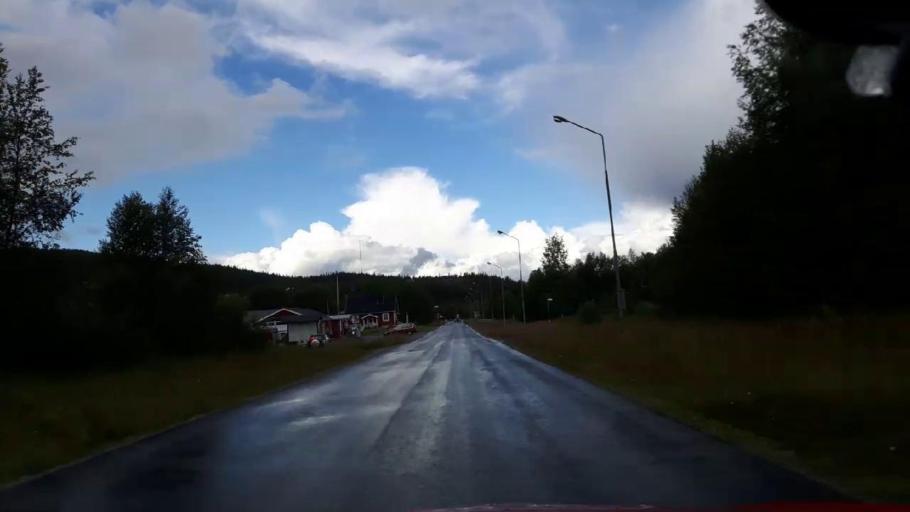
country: SE
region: Vaesterbotten
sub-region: Vilhelmina Kommun
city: Sjoberg
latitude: 64.9713
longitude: 15.3399
